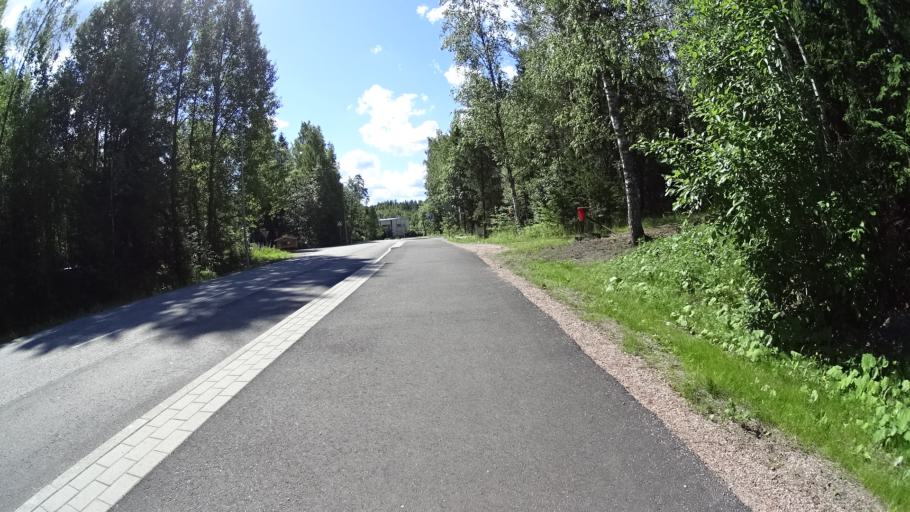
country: FI
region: Uusimaa
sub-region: Helsinki
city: Kirkkonummi
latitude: 60.2837
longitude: 24.4441
